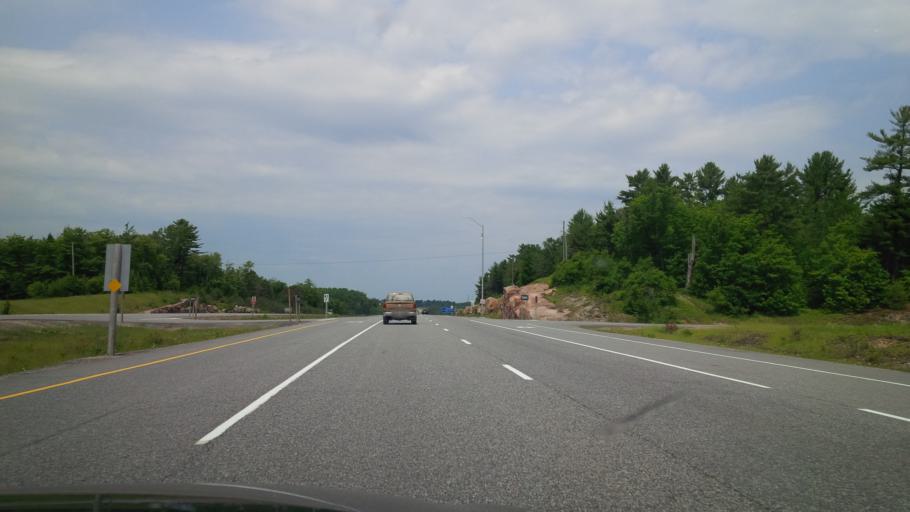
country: CA
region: Ontario
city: Huntsville
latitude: 45.4950
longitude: -79.2915
